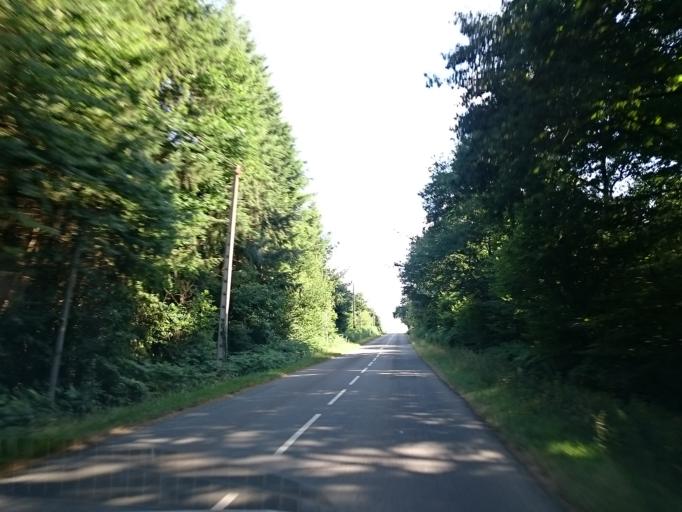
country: FR
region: Brittany
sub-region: Departement d'Ille-et-Vilaine
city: Pance
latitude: 47.9067
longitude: -1.6160
